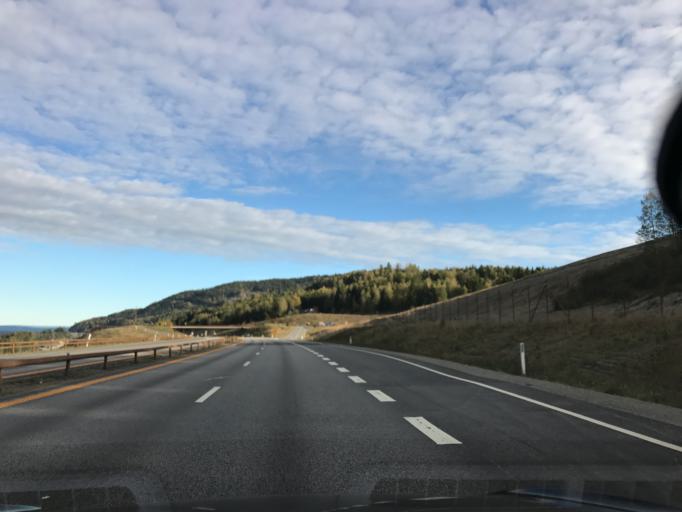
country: NO
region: Akershus
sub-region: Eidsvoll
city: Eidsvoll
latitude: 60.4102
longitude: 11.2398
